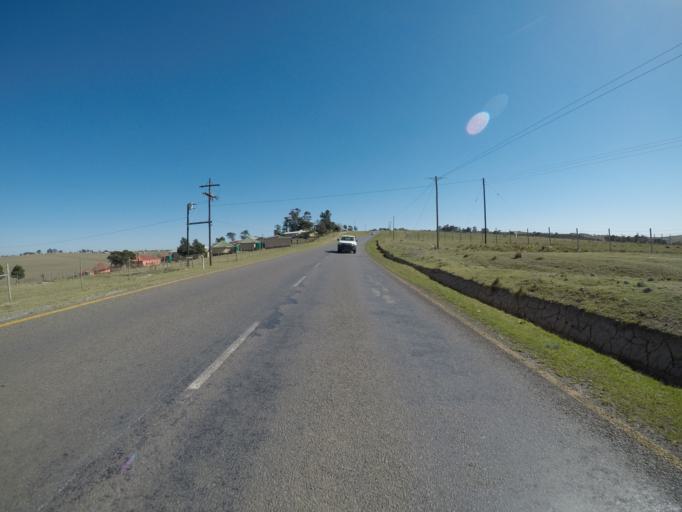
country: ZA
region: Eastern Cape
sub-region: OR Tambo District Municipality
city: Mthatha
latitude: -31.7961
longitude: 28.7449
